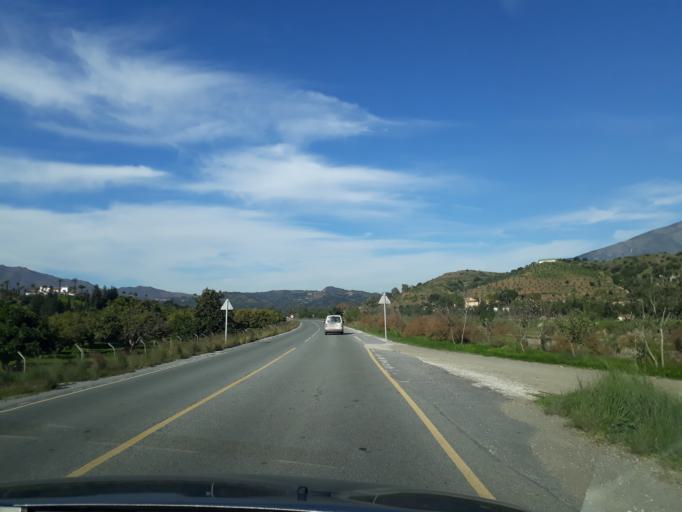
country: ES
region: Andalusia
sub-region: Provincia de Malaga
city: Fuengirola
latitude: 36.5443
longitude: -4.6879
